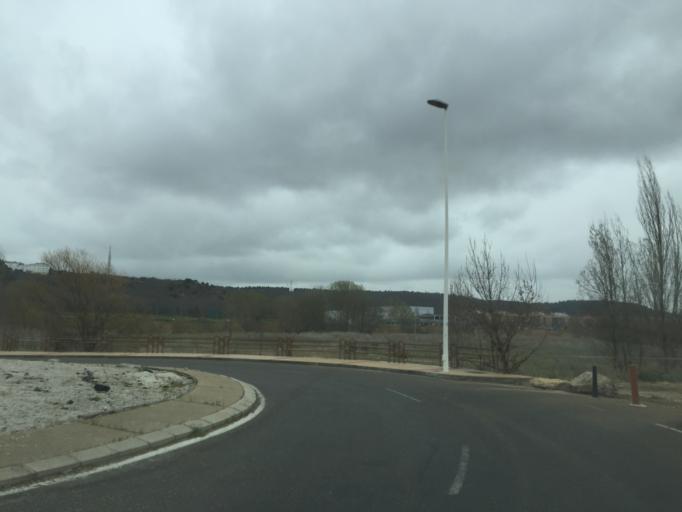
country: ES
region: Castille and Leon
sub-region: Provincia de Leon
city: San Andres del Rabanedo
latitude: 42.6372
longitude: -5.6077
